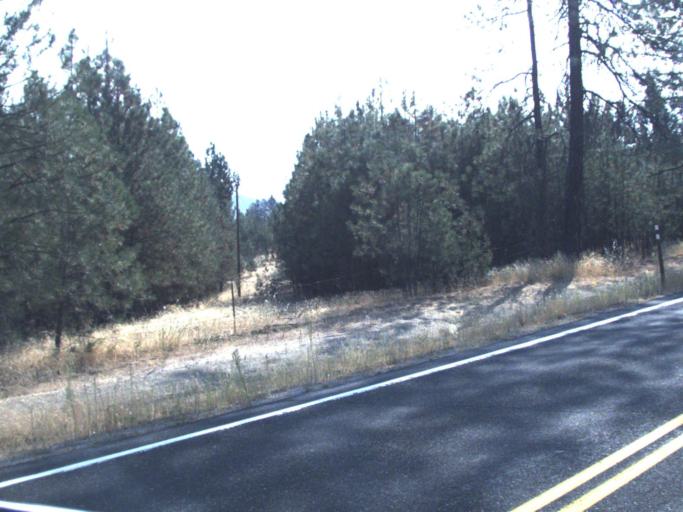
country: US
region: Washington
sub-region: Spokane County
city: Fairwood
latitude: 47.8168
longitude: -117.5820
